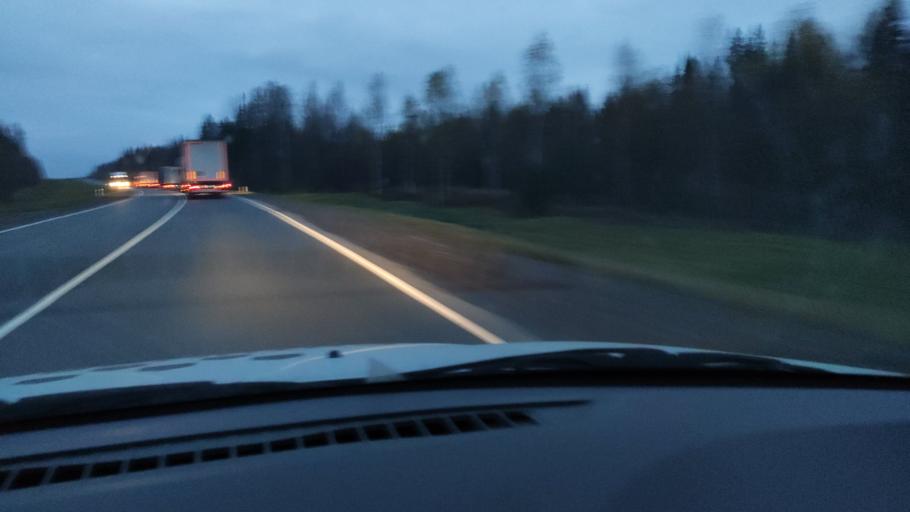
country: RU
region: Kirov
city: Kostino
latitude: 58.8270
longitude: 53.4270
